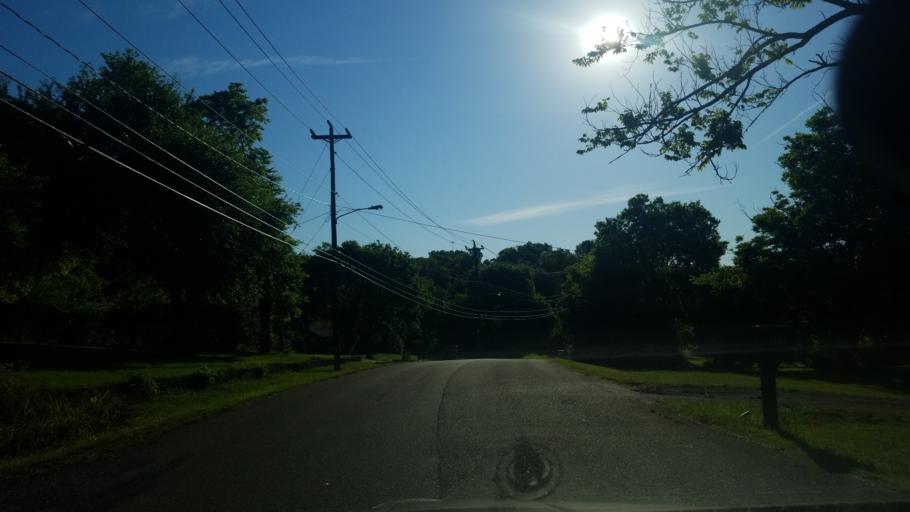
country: US
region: Tennessee
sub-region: Davidson County
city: Nashville
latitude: 36.2383
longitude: -86.7614
